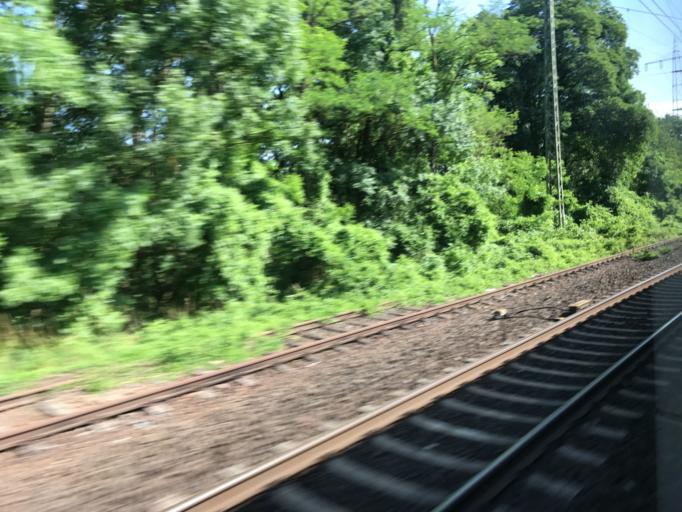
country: DE
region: Hesse
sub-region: Regierungsbezirk Darmstadt
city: Eltville
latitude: 50.0059
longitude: 8.1340
